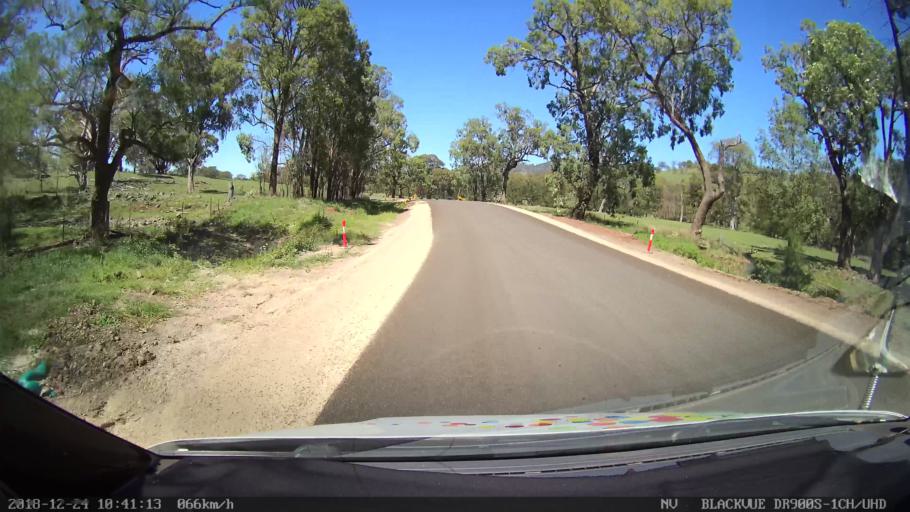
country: AU
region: New South Wales
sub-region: Upper Hunter Shire
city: Merriwa
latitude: -31.8672
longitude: 150.4609
